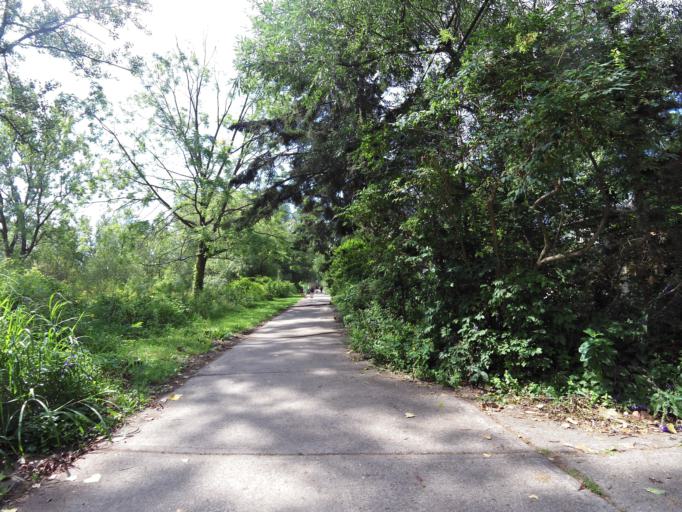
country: CA
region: Ontario
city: Toronto
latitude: 43.6324
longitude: -79.3534
